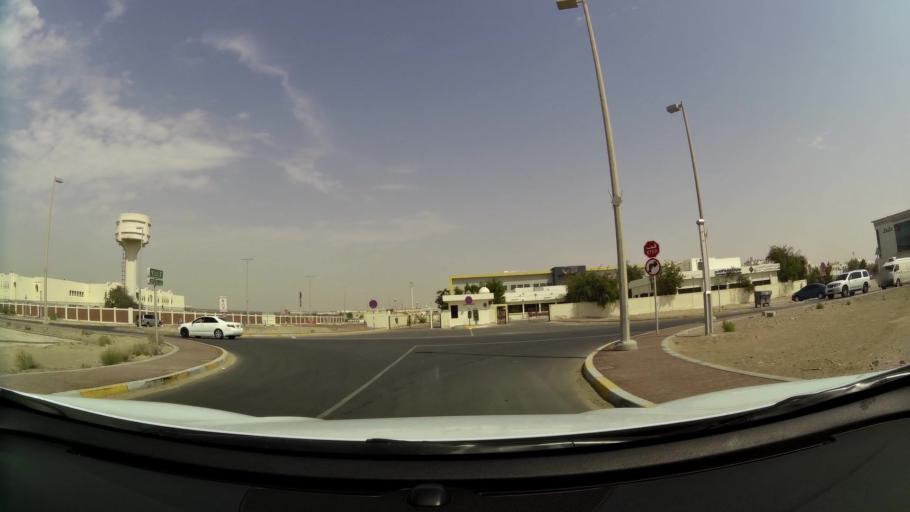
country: AE
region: Abu Dhabi
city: Abu Dhabi
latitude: 24.2970
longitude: 54.6343
